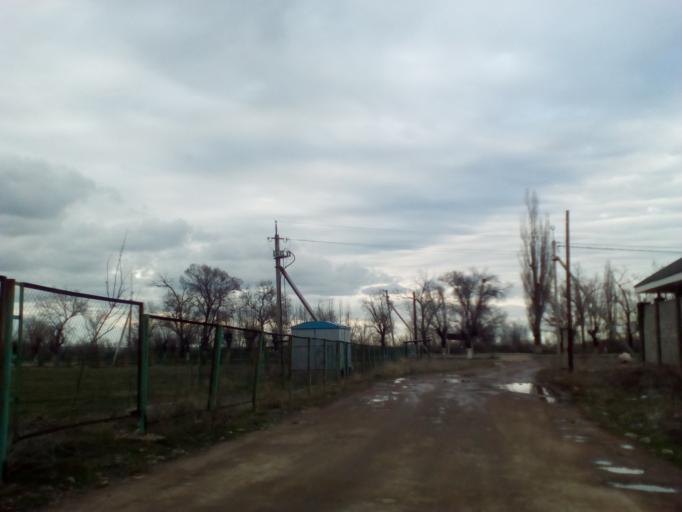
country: KZ
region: Almaty Oblysy
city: Burunday
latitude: 43.1811
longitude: 76.4001
